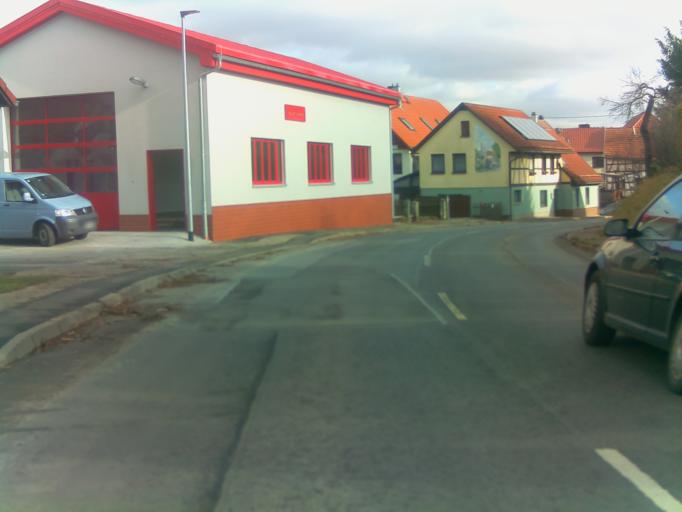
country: DE
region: Thuringia
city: Reurieth
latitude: 50.4107
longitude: 10.6817
